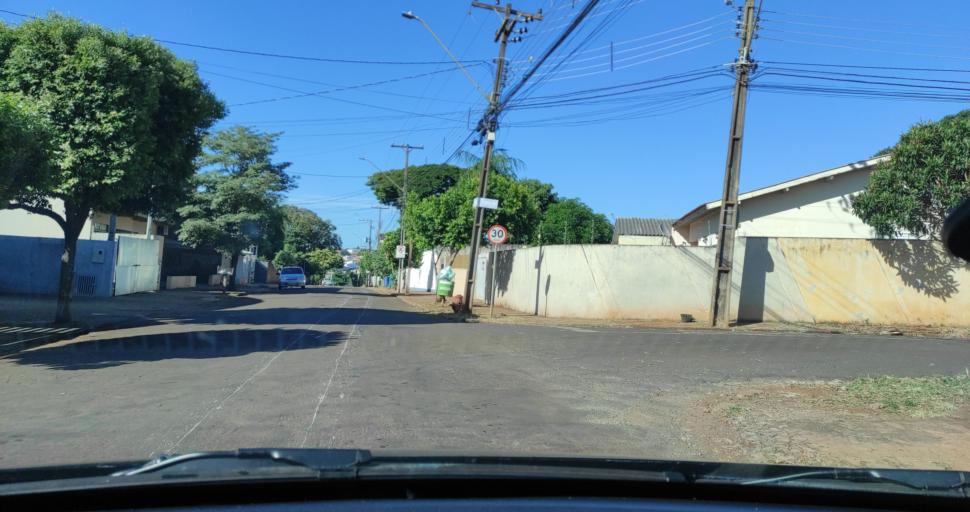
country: BR
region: Parana
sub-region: Ibipora
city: Ibipora
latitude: -23.2591
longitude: -51.0583
